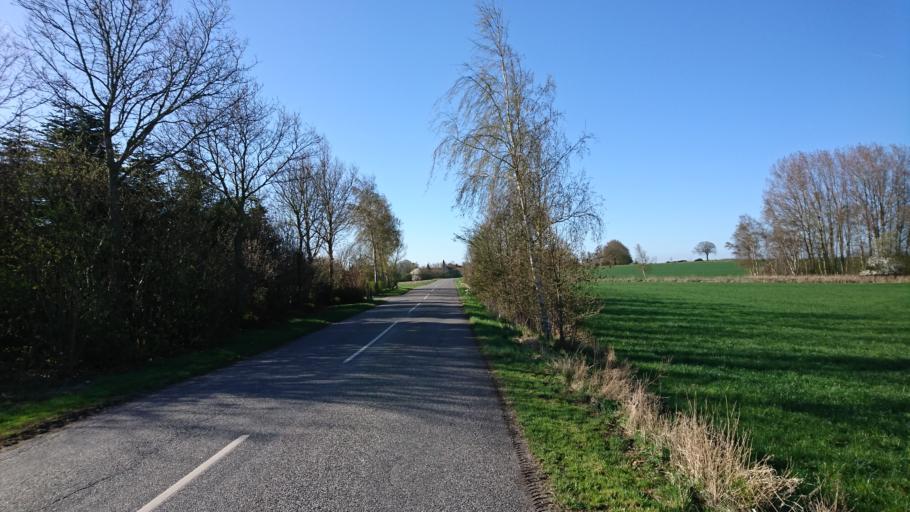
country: DK
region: Capital Region
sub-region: Frederikssund Kommune
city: Skibby
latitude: 55.7284
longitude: 11.9289
